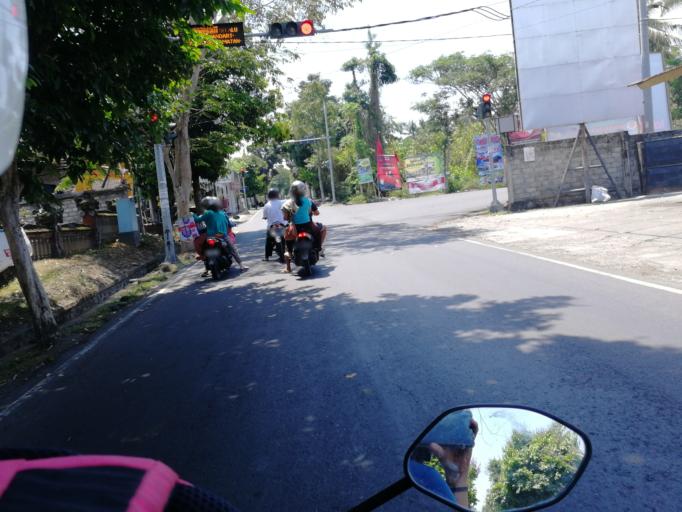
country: ID
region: Bali
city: Banjar Beji
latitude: -8.4475
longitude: 115.5879
